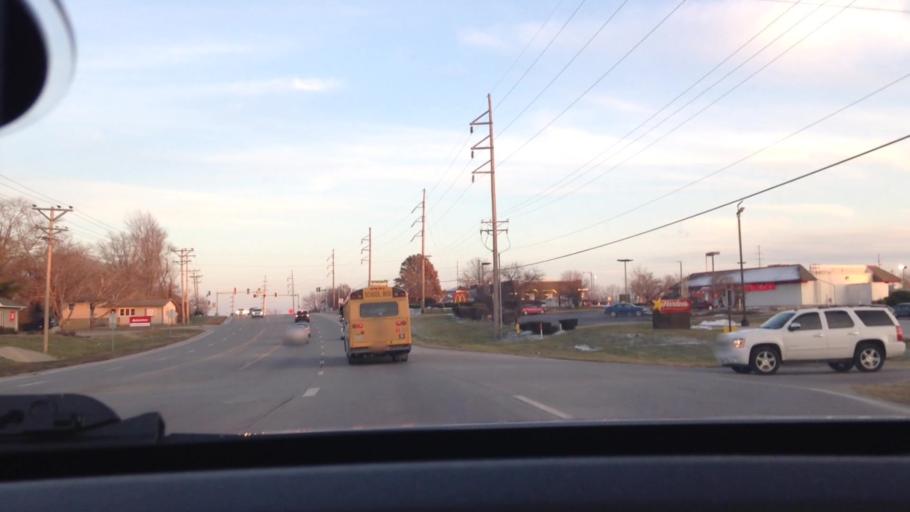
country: US
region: Missouri
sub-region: Clay County
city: Liberty
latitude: 39.2380
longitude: -94.4354
